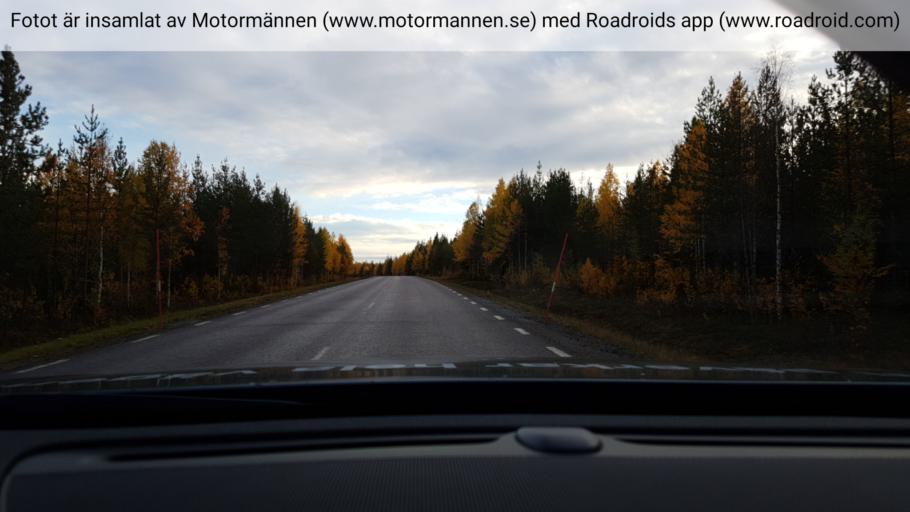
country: SE
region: Norrbotten
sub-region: Overkalix Kommun
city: OEverkalix
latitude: 66.8650
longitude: 22.7550
